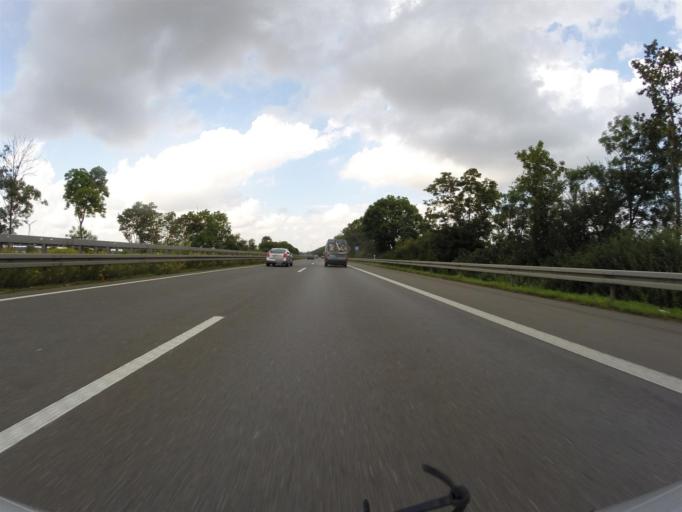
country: DE
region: North Rhine-Westphalia
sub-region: Regierungsbezirk Detmold
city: Wunnenberg
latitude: 51.5554
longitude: 8.7945
